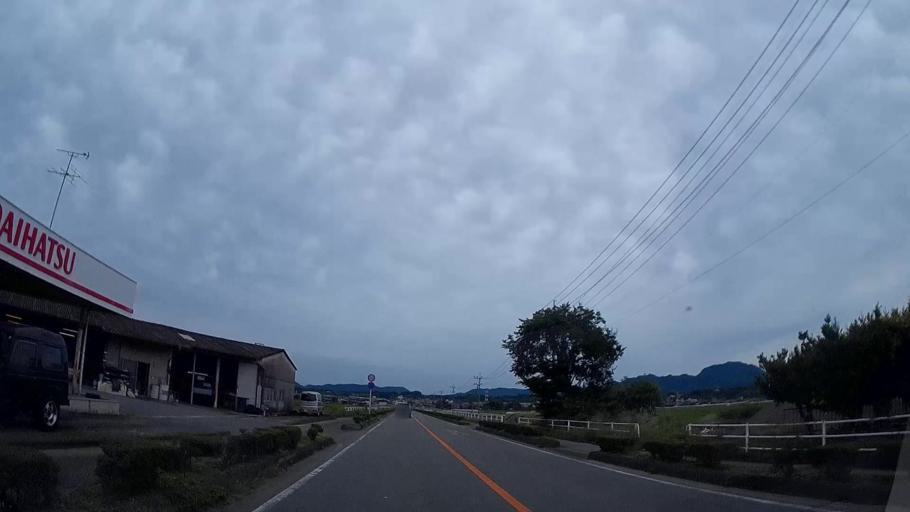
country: JP
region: Kumamoto
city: Kikuchi
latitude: 32.9631
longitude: 130.8153
